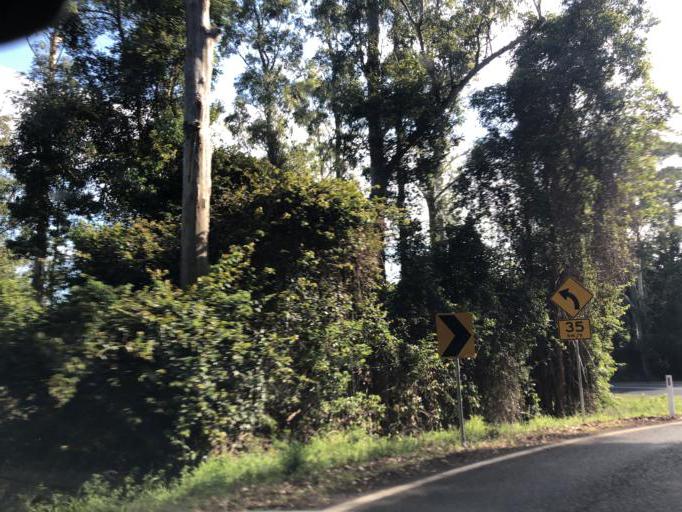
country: AU
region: New South Wales
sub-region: Coffs Harbour
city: Coffs Harbour
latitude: -30.2630
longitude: 153.1310
